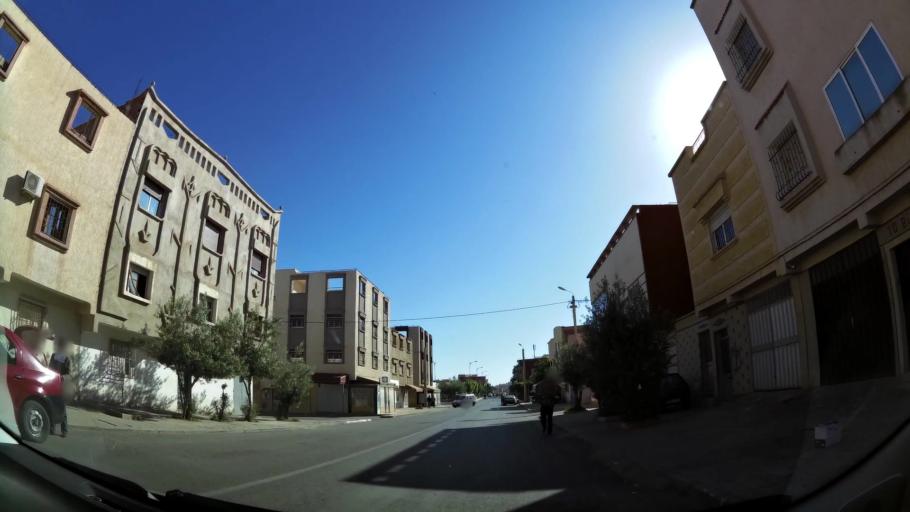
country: MA
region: Oriental
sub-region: Oujda-Angad
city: Oujda
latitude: 34.6529
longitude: -1.8962
